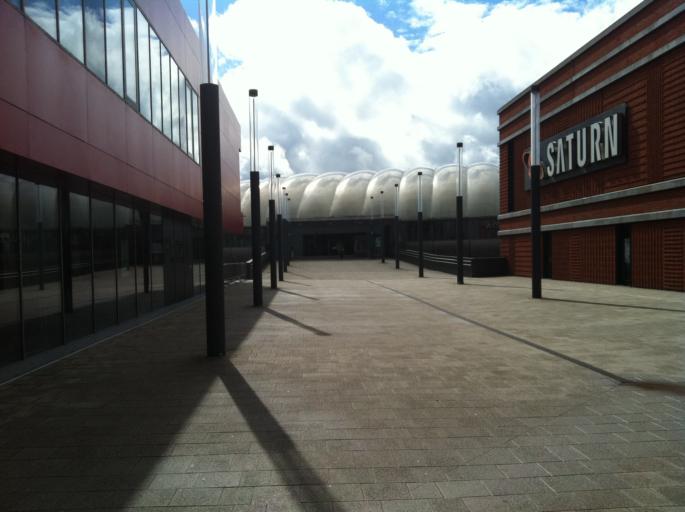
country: FR
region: Lorraine
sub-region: Departement de la Moselle
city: Russange
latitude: 49.5000
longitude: 5.9467
